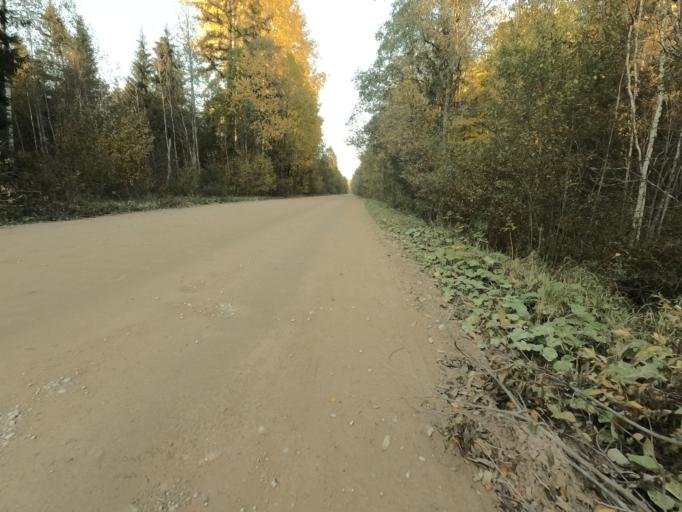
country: RU
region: Leningrad
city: Lyuban'
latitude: 58.9872
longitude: 31.1003
